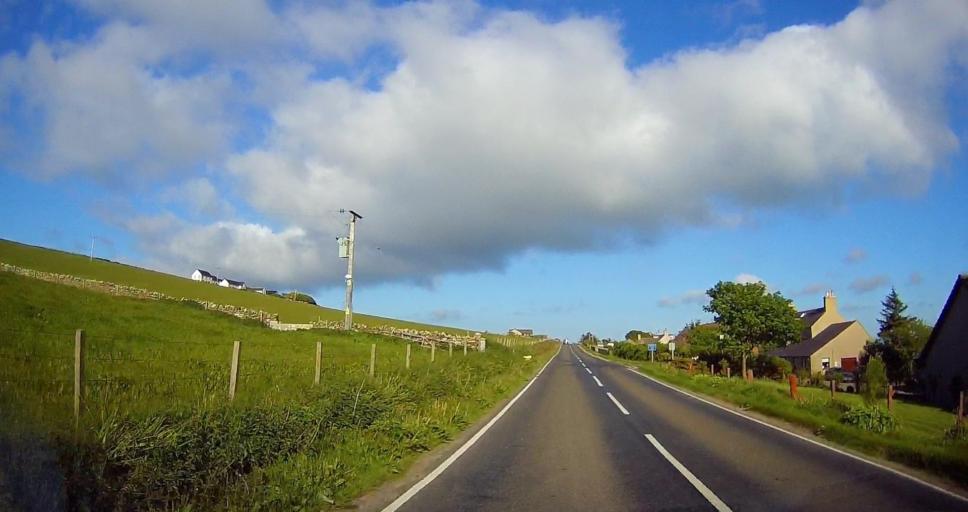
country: GB
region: Scotland
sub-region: Orkney Islands
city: Orkney
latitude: 58.9788
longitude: -3.0195
